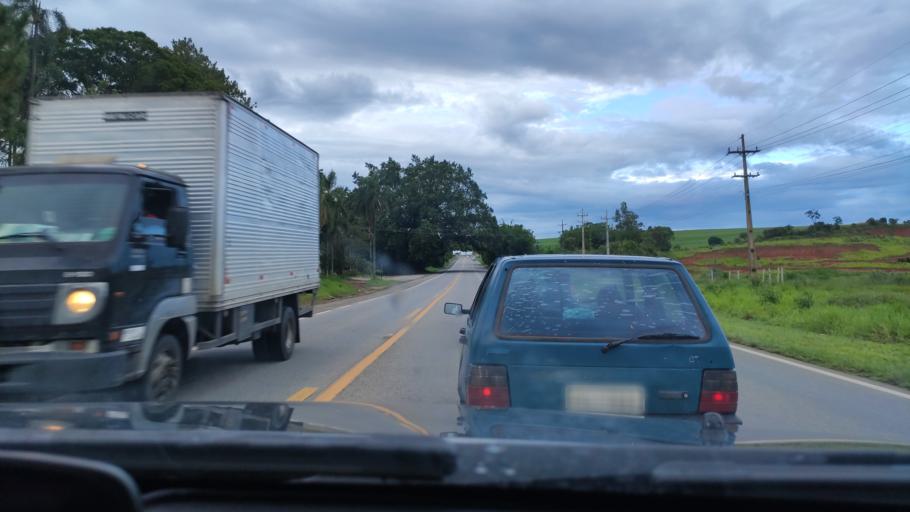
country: BR
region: Sao Paulo
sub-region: Braganca Paulista
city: Braganca Paulista
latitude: -22.8913
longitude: -46.5415
